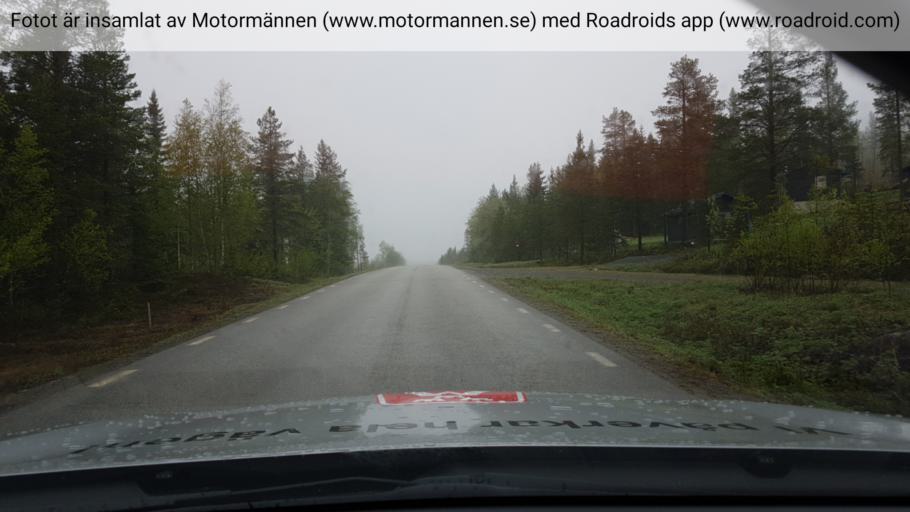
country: SE
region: Jaemtland
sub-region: Bergs Kommun
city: Hoverberg
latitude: 63.0312
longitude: 14.0513
